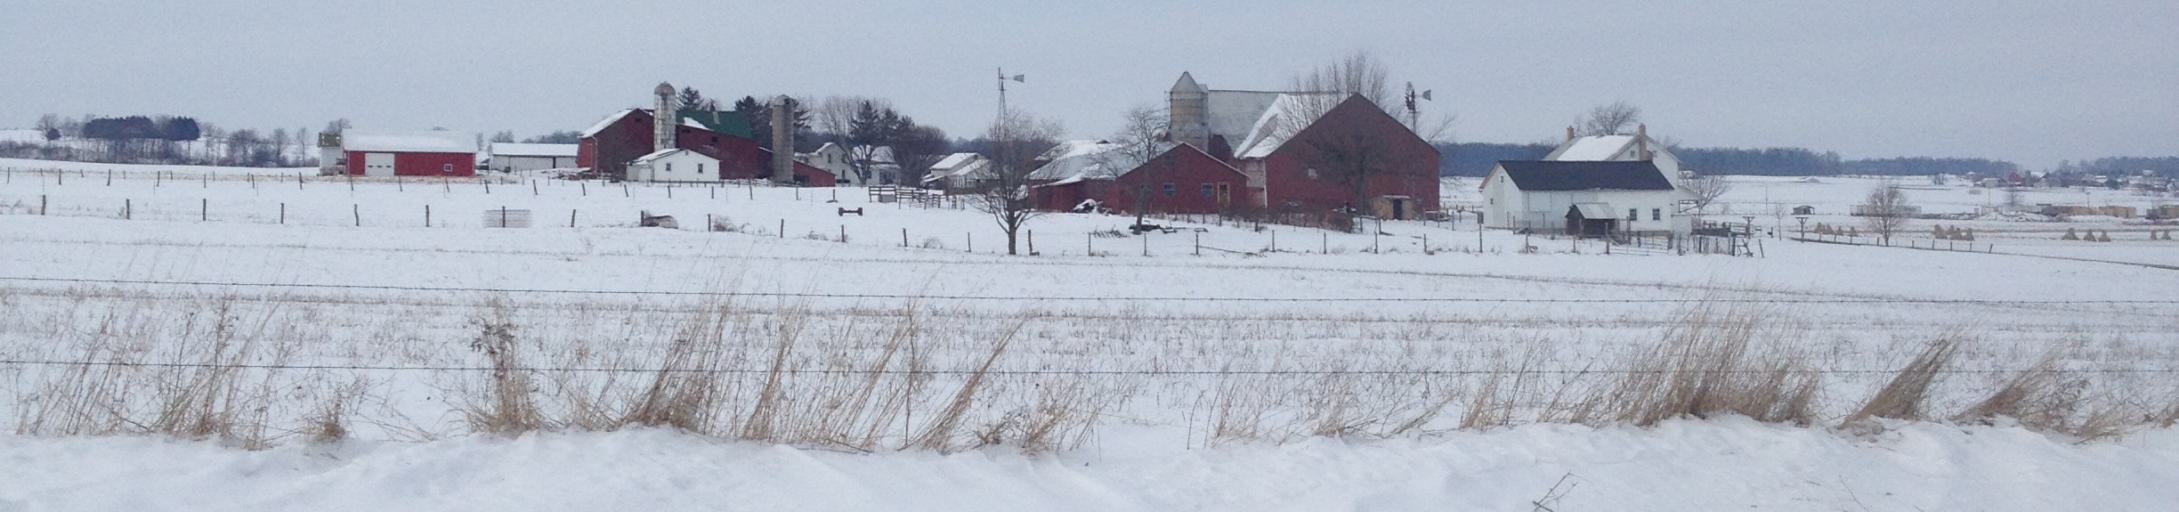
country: US
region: Ohio
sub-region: Wayne County
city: Apple Creek
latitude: 40.6906
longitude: -81.7460
